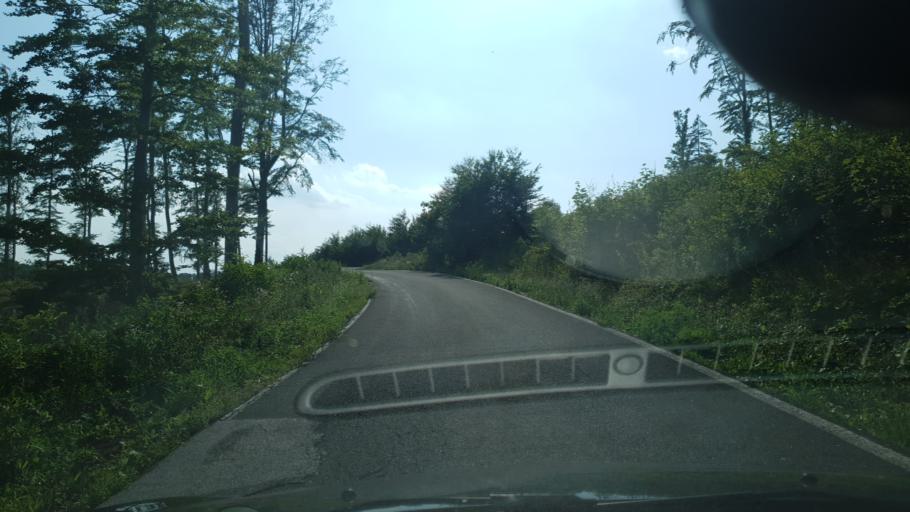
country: HR
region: Grad Zagreb
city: Kasina
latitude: 45.8906
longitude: 15.9578
